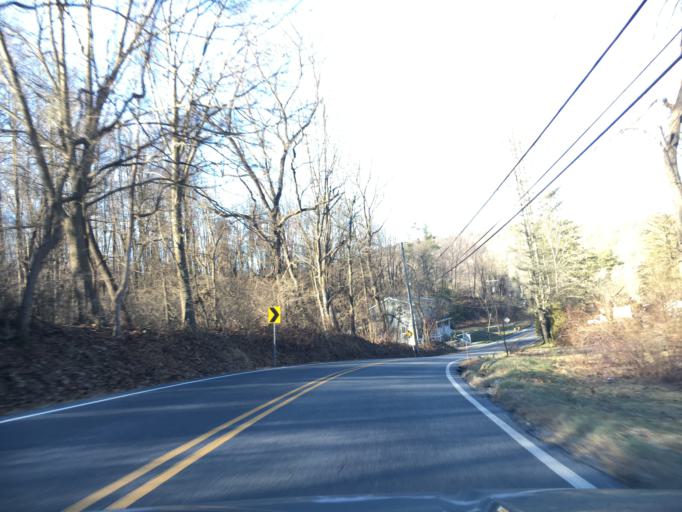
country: US
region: Pennsylvania
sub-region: Berks County
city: South Temple
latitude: 40.4076
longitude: -75.8764
